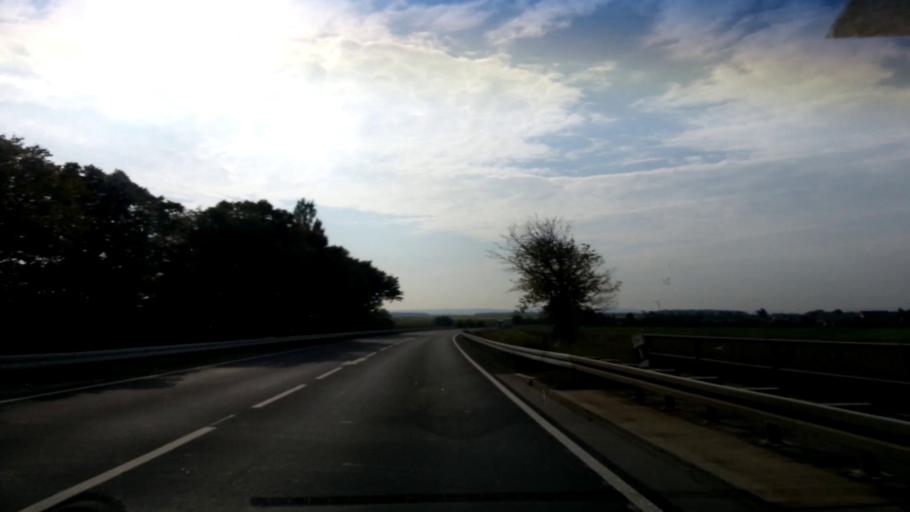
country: DE
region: Bavaria
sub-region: Regierungsbezirk Unterfranken
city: Gerolzhofen
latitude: 49.8766
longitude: 10.3600
